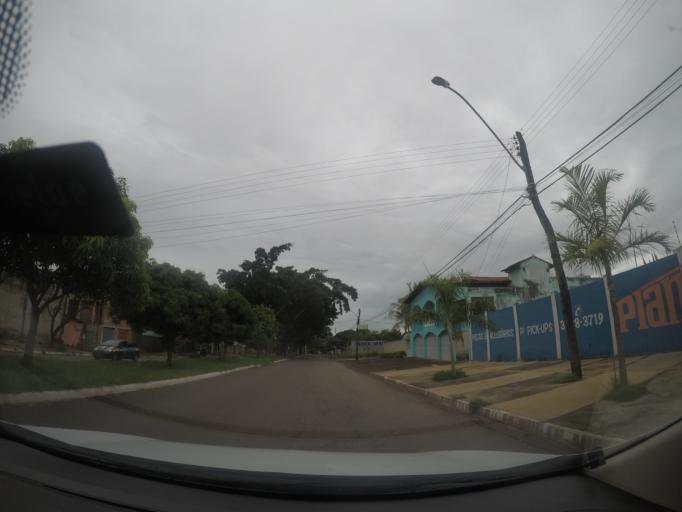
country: BR
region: Goias
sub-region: Goiania
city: Goiania
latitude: -16.6699
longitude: -49.3246
